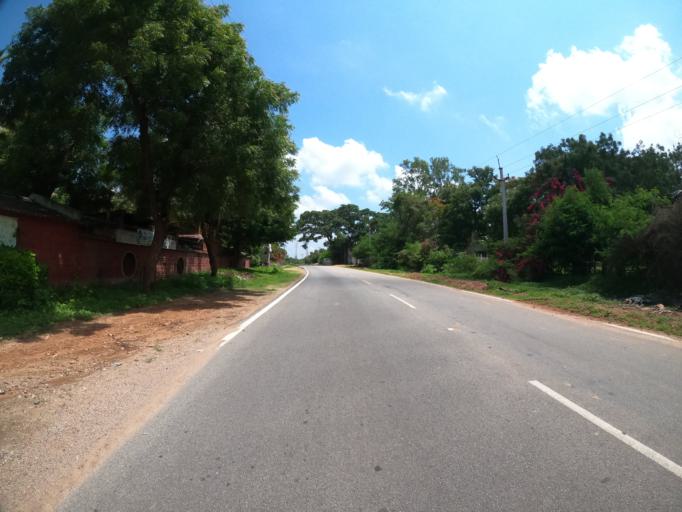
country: IN
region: Telangana
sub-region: Rangareddi
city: Sriramnagar
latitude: 17.3690
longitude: 78.3250
